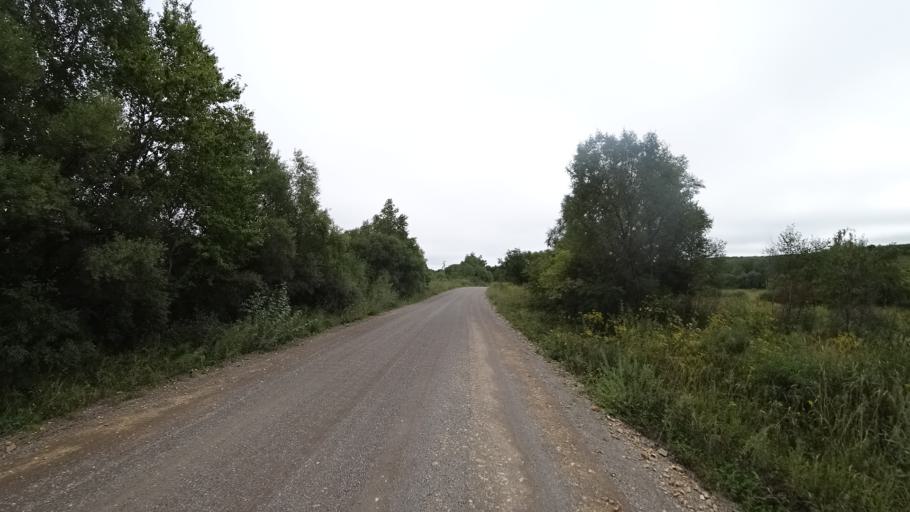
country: RU
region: Primorskiy
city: Ivanovka
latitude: 44.0467
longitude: 132.4917
